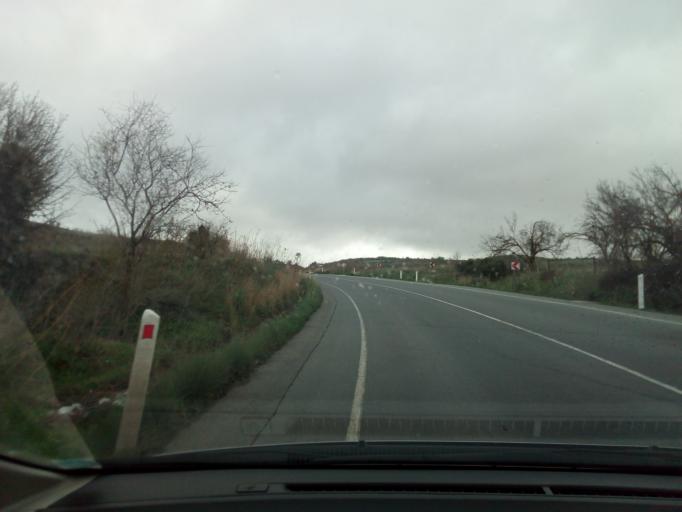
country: CY
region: Pafos
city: Tala
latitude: 34.9079
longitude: 32.4662
